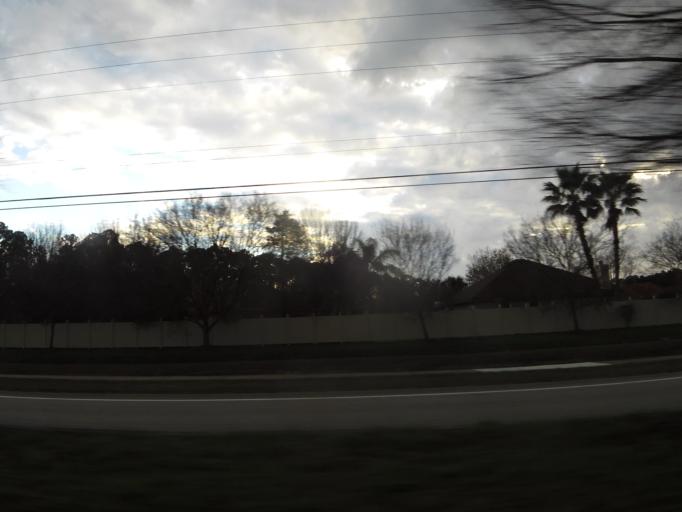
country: US
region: Florida
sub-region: Saint Johns County
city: Fruit Cove
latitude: 30.1847
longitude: -81.5743
